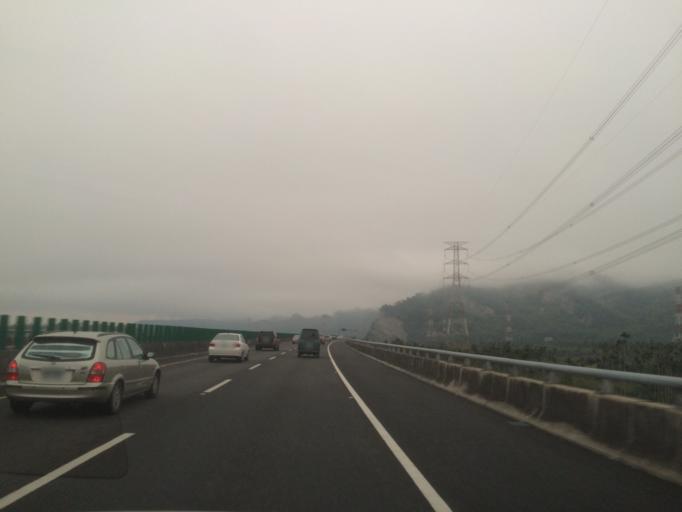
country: TW
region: Taiwan
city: Zhongxing New Village
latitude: 23.9876
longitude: 120.7561
